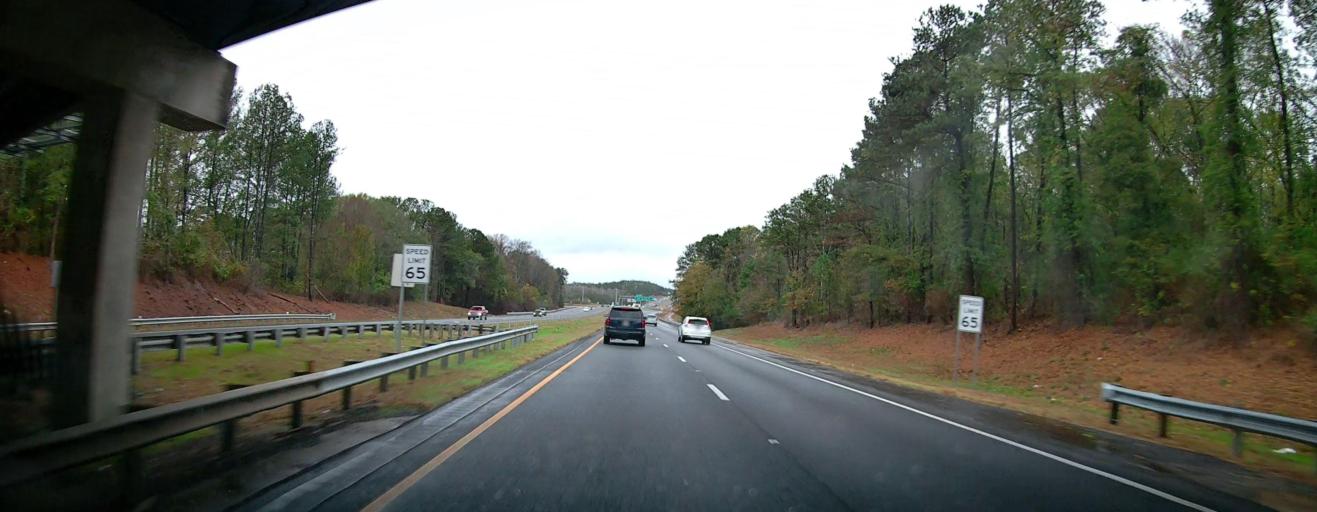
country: US
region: Georgia
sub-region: Clarke County
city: Athens
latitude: 33.9554
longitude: -83.3497
